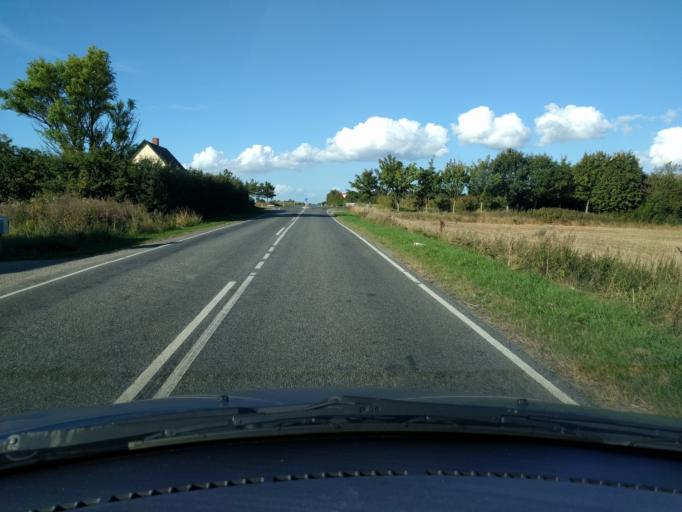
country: DK
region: South Denmark
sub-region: Assens Kommune
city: Assens
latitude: 55.2607
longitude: 9.9809
